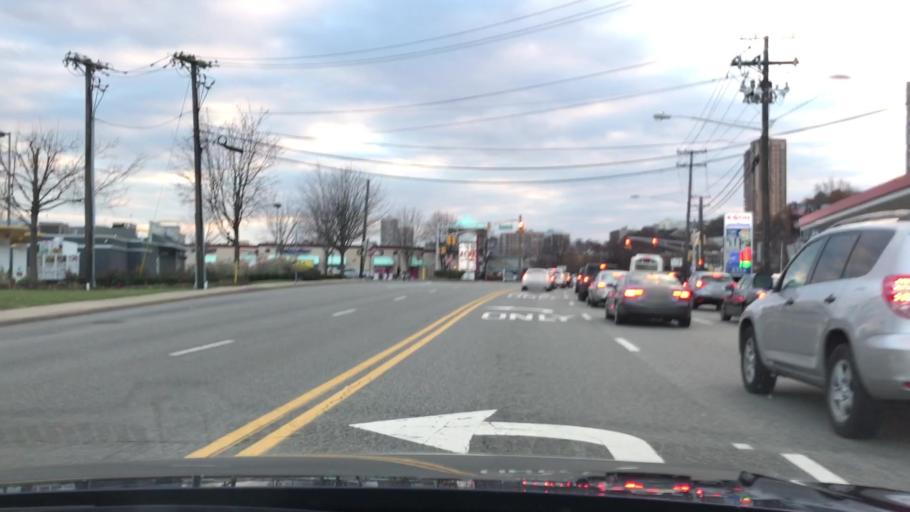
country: US
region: New Jersey
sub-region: Bergen County
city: Cliffside Park
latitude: 40.8143
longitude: -73.9836
